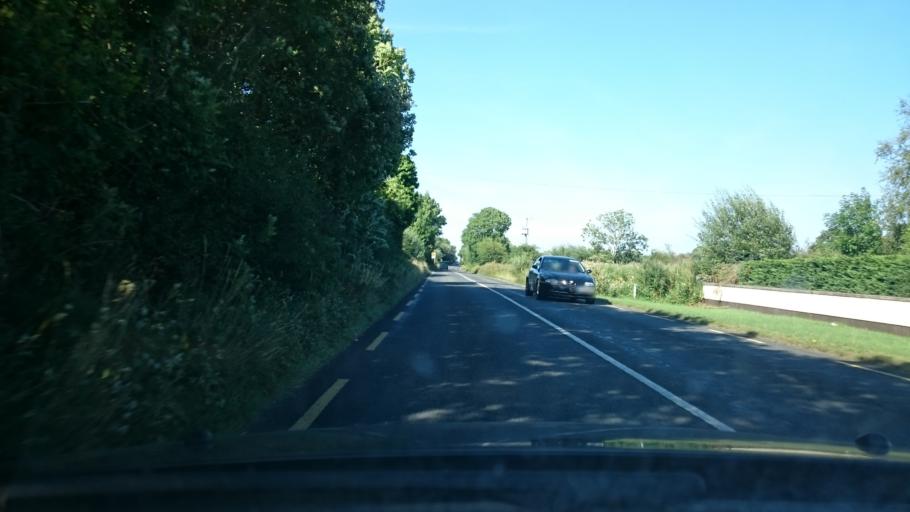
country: IE
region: Leinster
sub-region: Kilkenny
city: Graiguenamanagh
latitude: 52.5546
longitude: -6.9559
